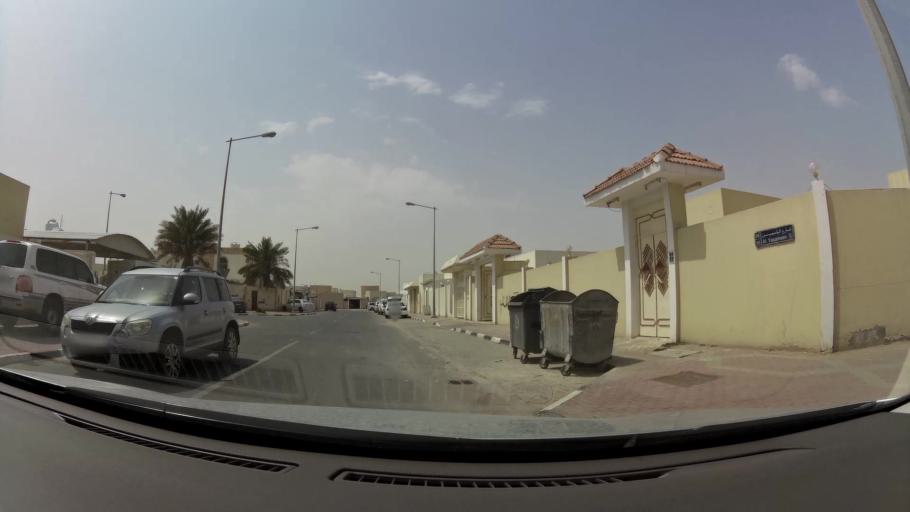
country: QA
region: Baladiyat ar Rayyan
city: Ar Rayyan
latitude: 25.2427
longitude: 51.4260
